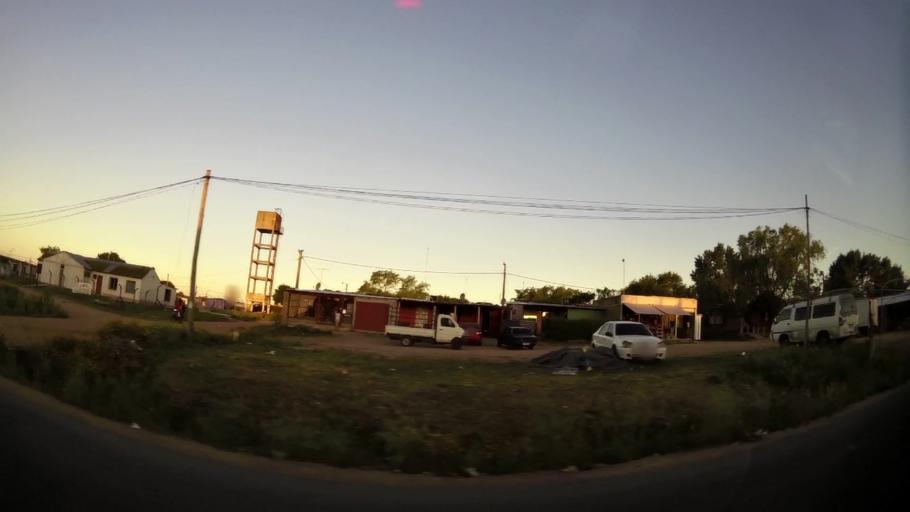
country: UY
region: Montevideo
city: Montevideo
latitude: -34.8295
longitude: -56.1681
